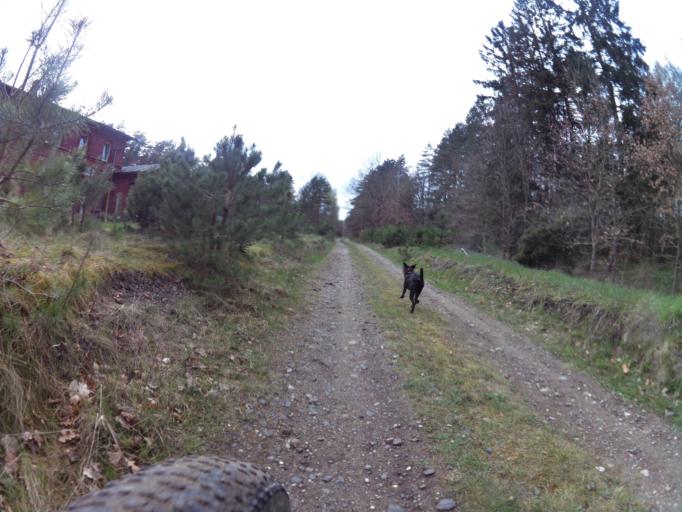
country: PL
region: West Pomeranian Voivodeship
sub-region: Powiat slawienski
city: Slawno
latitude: 54.3233
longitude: 16.7633
